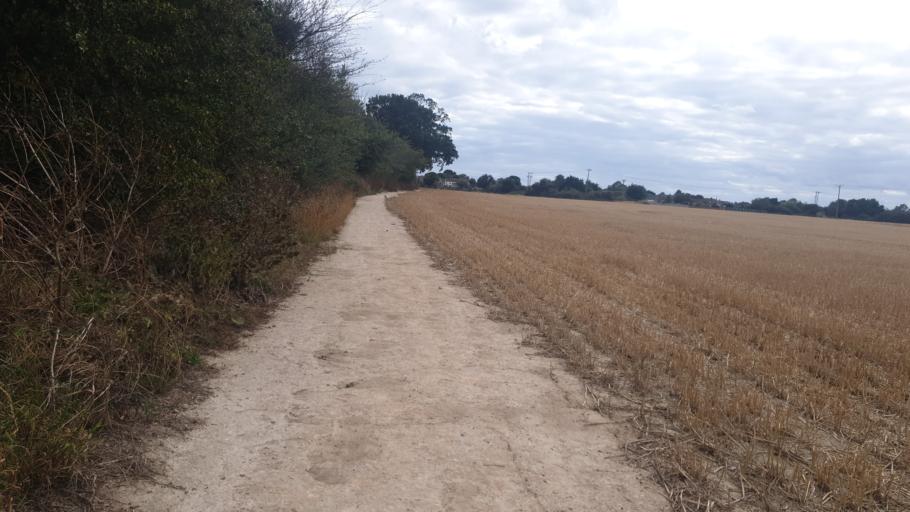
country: GB
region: England
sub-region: Essex
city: Frinton-on-Sea
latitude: 51.8476
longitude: 1.2355
